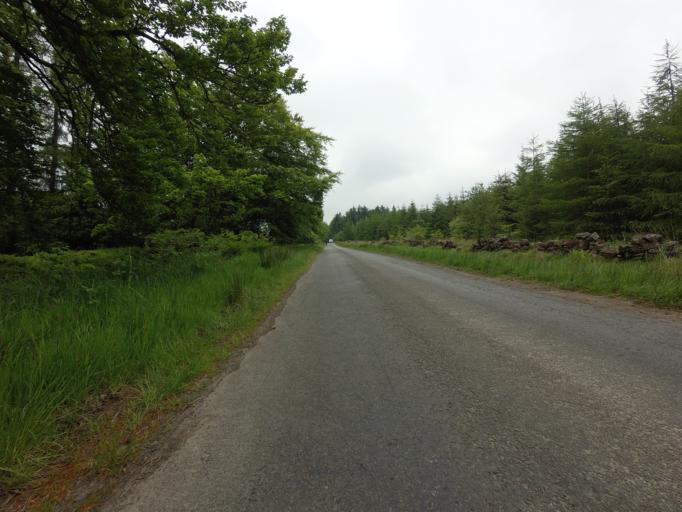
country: GB
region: Scotland
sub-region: Fife
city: Townhill
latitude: 56.1318
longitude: -3.4427
